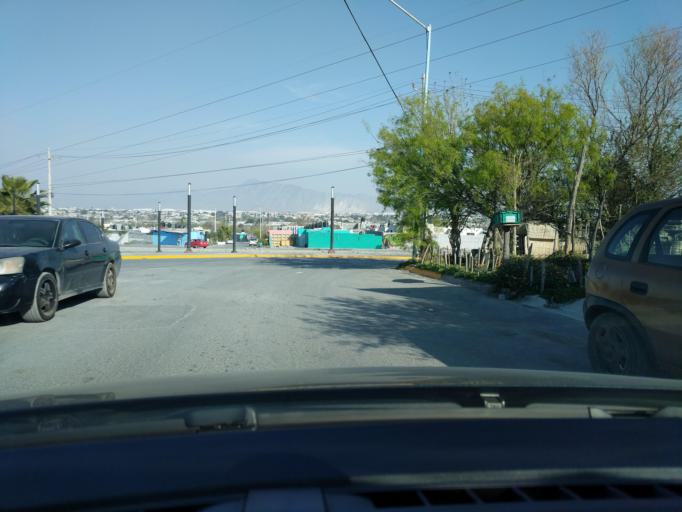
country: MX
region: Coahuila
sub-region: Ramos Arizpe
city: Ramos Arizpe
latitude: 25.5457
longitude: -100.9672
